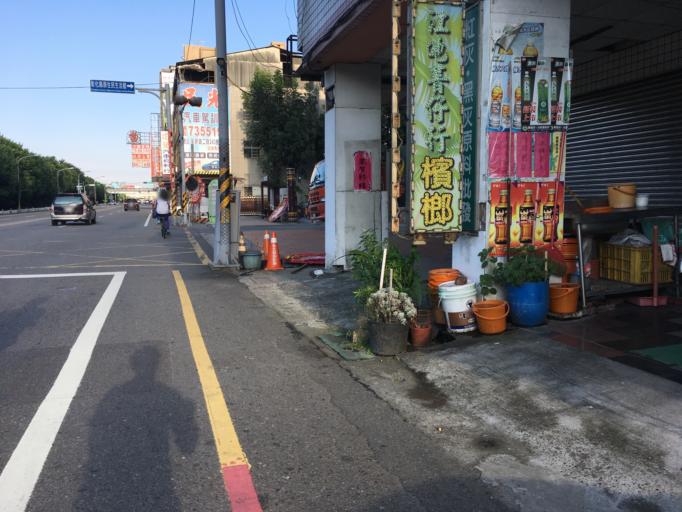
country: TW
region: Taiwan
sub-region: Changhua
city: Chang-hua
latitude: 24.0864
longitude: 120.5596
